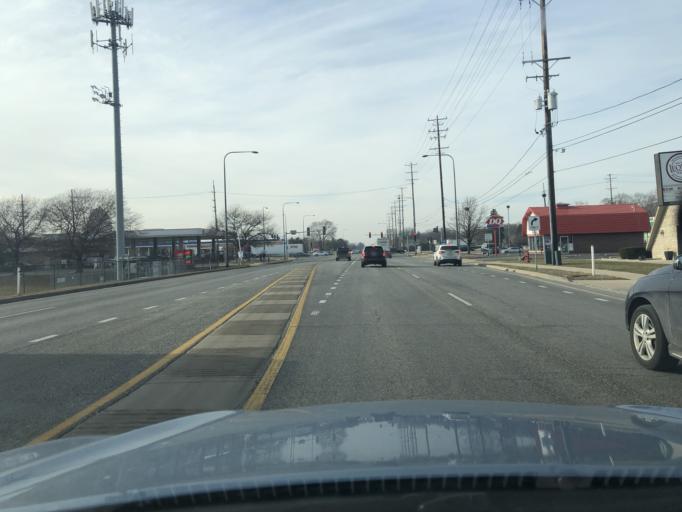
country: US
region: Illinois
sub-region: DuPage County
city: Itasca
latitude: 41.9926
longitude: -88.0012
